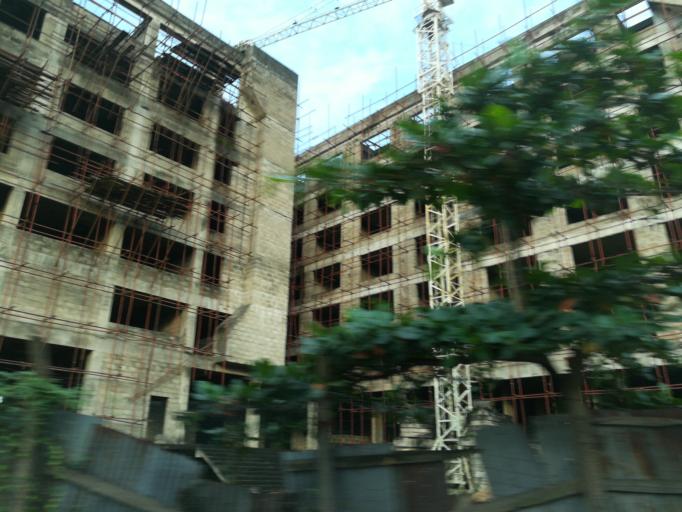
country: NG
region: Lagos
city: Ikeja
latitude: 6.5857
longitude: 3.3338
